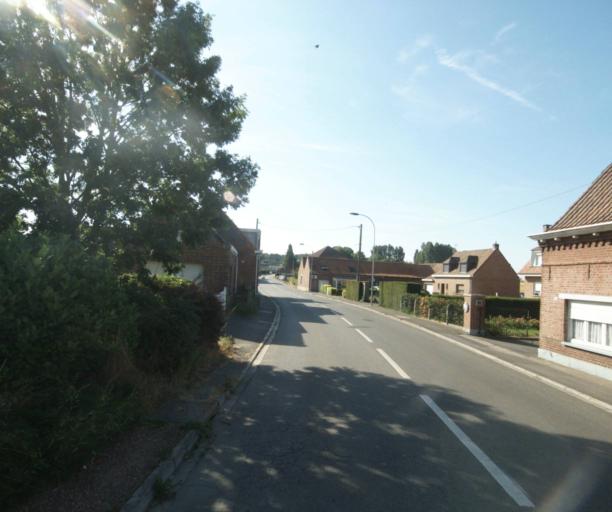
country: FR
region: Nord-Pas-de-Calais
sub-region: Departement du Nord
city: Halluin
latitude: 50.7708
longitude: 3.1402
